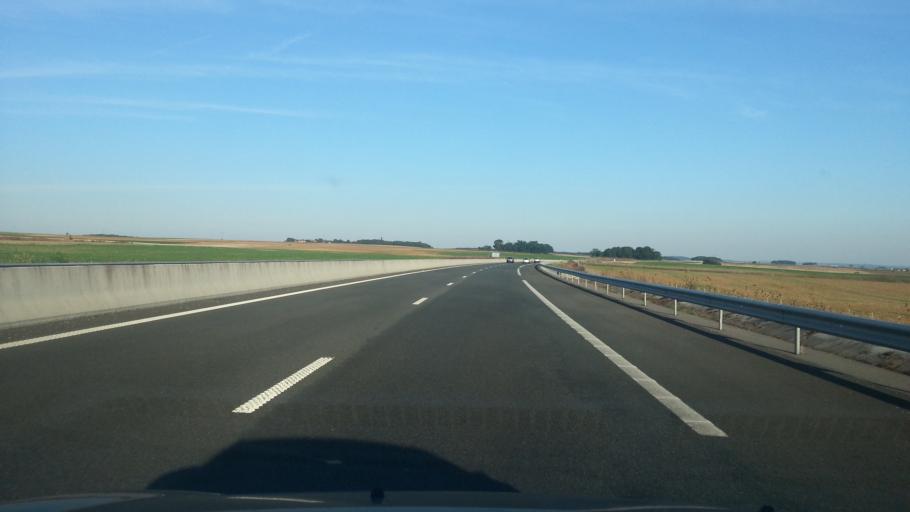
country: FR
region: Picardie
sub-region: Departement de l'Oise
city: Catenoy
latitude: 49.3848
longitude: 2.4879
